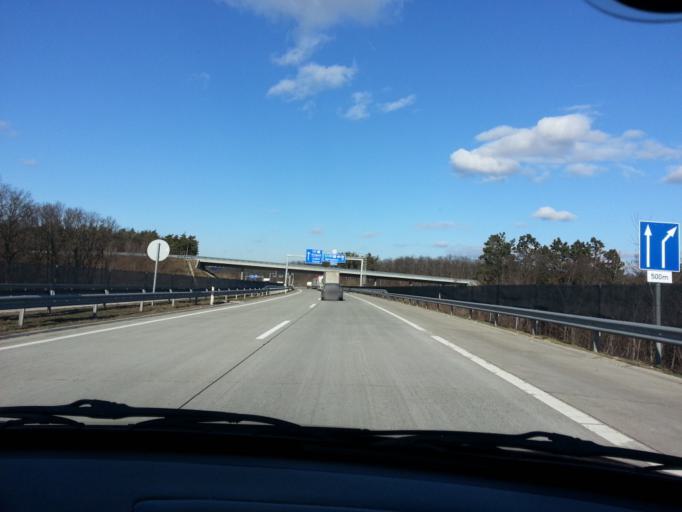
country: HU
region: Pest
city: Szada
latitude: 47.6003
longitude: 19.3210
